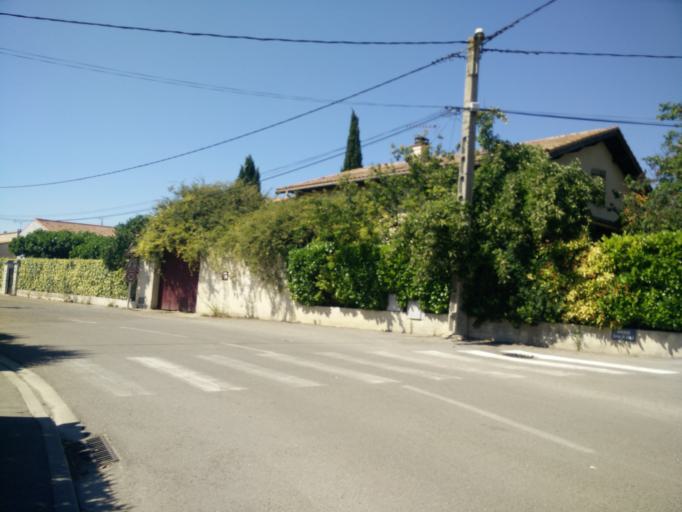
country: FR
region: Languedoc-Roussillon
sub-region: Departement du Gard
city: Vestric-et-Candiac
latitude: 43.7407
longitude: 4.2574
